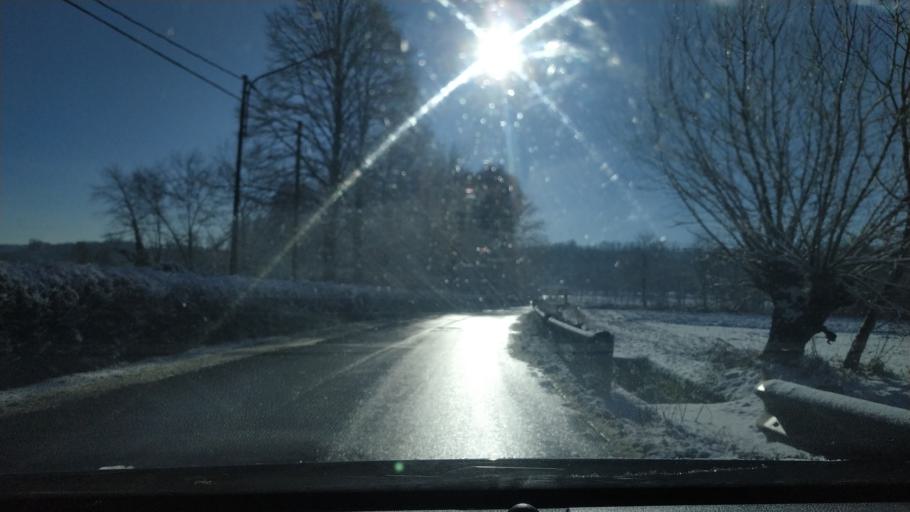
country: IT
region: Piedmont
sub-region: Provincia di Torino
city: Candia Canavese
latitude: 45.3214
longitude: 7.8973
